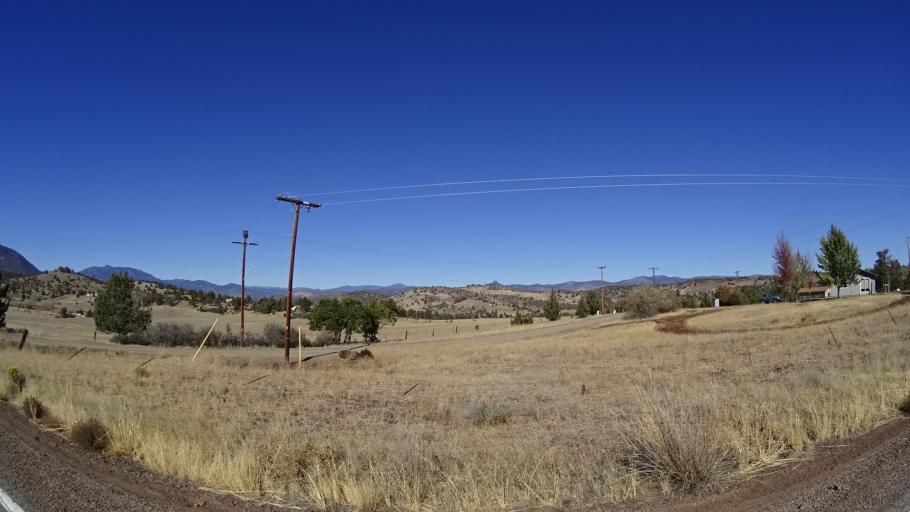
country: US
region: California
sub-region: Siskiyou County
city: Montague
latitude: 41.8816
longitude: -122.4157
